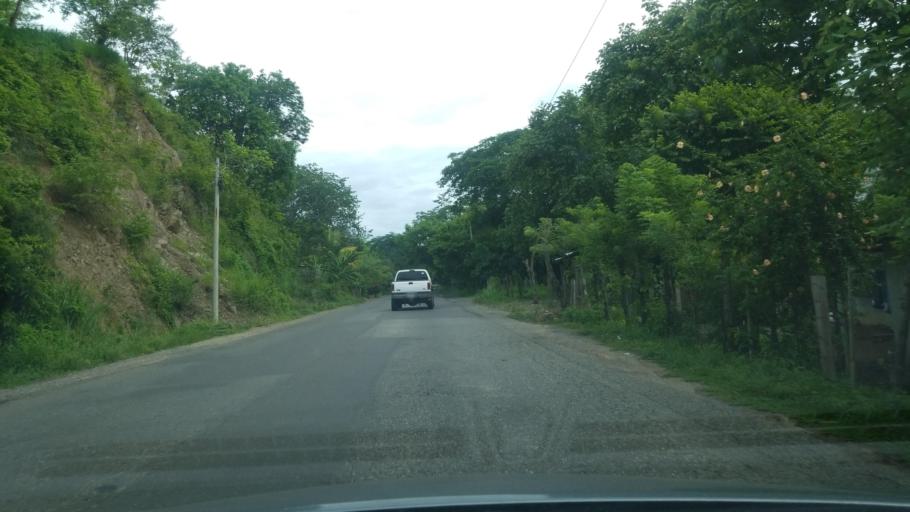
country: HN
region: Santa Barbara
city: Camalote
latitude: 15.3281
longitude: -88.2932
